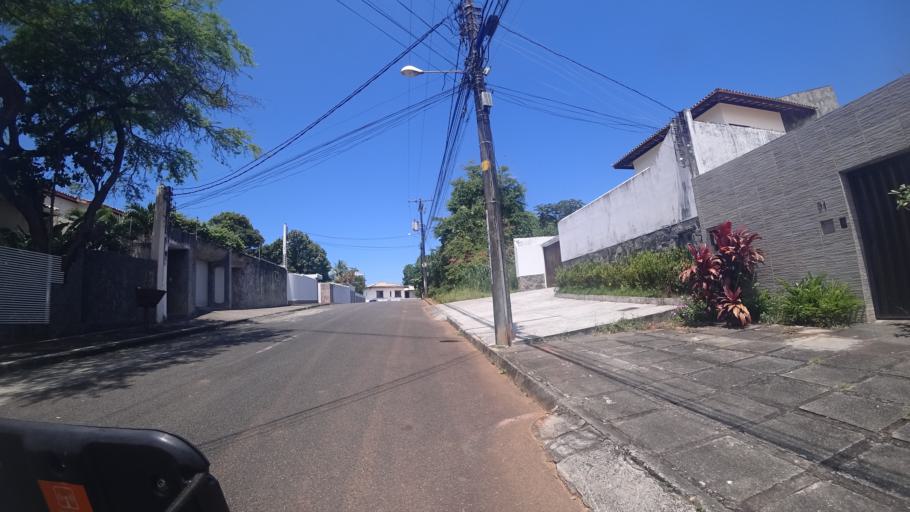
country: BR
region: Bahia
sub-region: Salvador
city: Salvador
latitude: -12.9942
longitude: -38.4659
